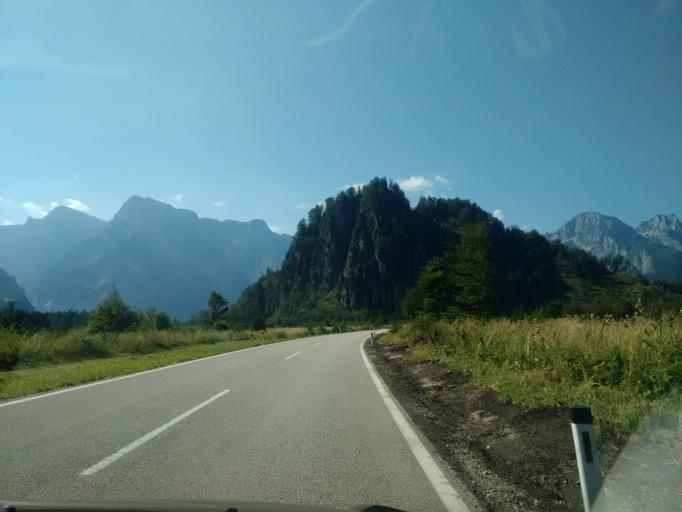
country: AT
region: Upper Austria
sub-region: Politischer Bezirk Gmunden
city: Gruenau im Almtal
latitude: 47.7645
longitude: 13.9555
